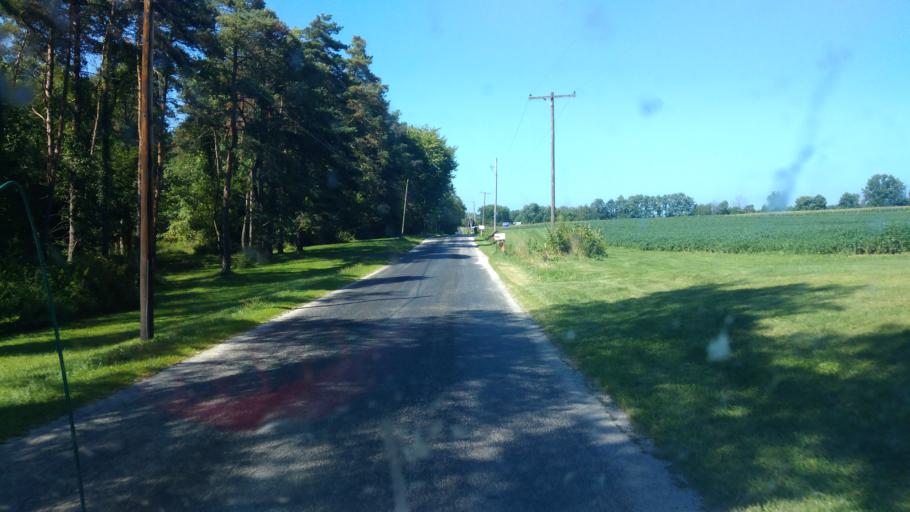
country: US
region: Ohio
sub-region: Ashland County
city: Ashland
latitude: 40.9050
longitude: -82.2623
